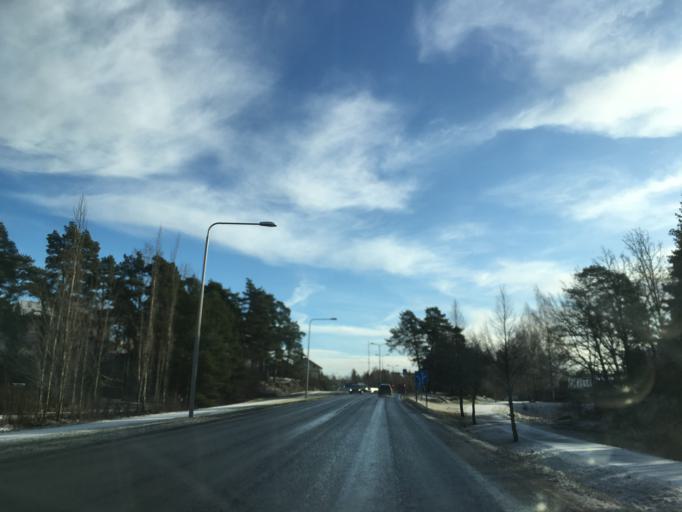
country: FI
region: Varsinais-Suomi
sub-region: Turku
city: Raisio
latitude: 60.4791
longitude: 22.1930
